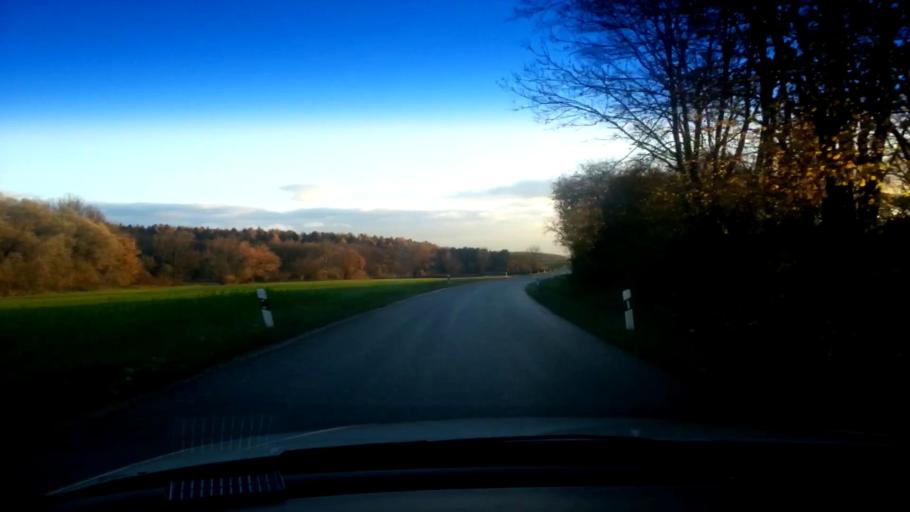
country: DE
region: Bavaria
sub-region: Upper Franconia
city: Buttenheim
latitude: 49.8241
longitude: 11.0563
